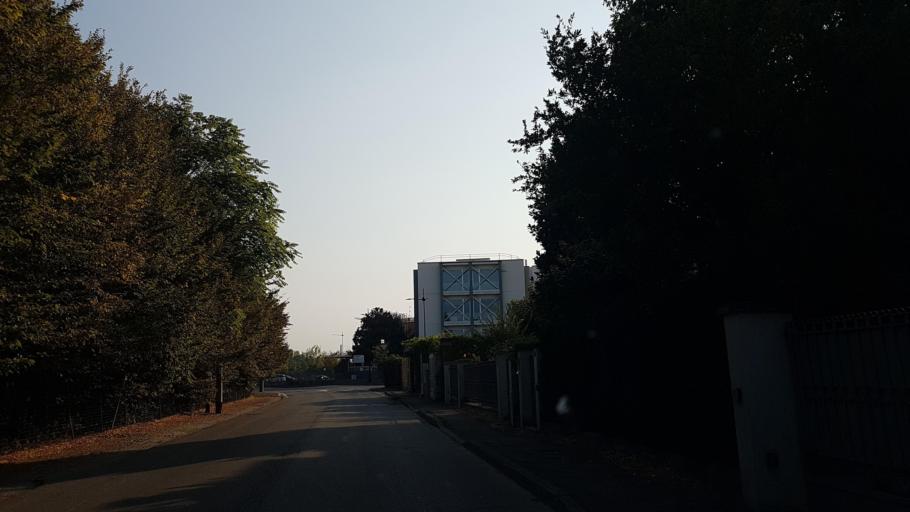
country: IT
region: Emilia-Romagna
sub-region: Provincia di Parma
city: Vicofertile
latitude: 44.7810
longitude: 10.2827
